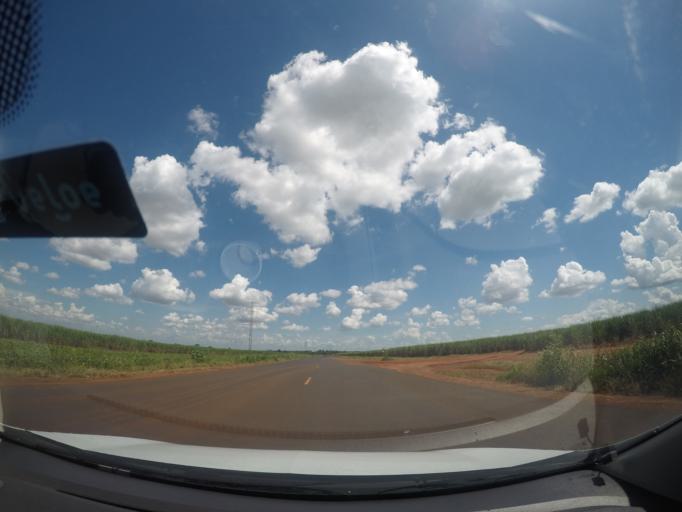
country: BR
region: Minas Gerais
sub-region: Frutal
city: Frutal
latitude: -19.8273
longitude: -48.7335
